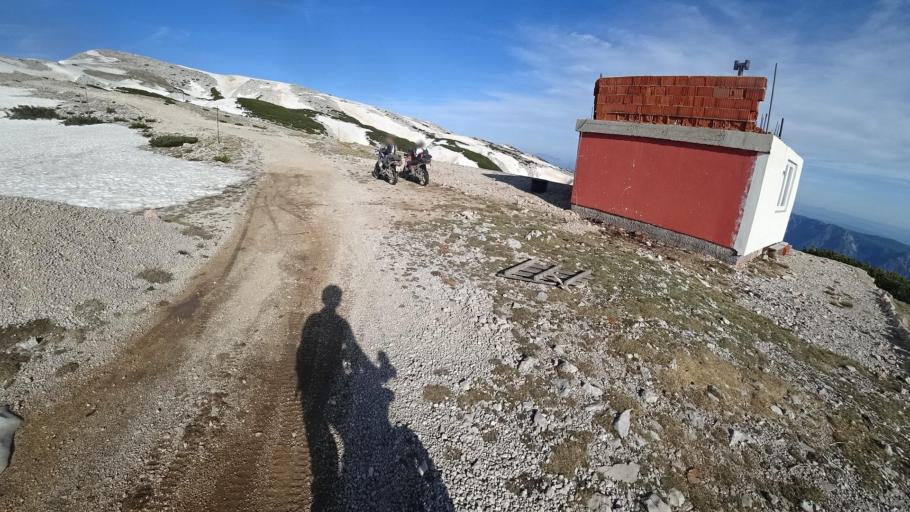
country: BA
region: Federation of Bosnia and Herzegovina
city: Kocerin
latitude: 43.5998
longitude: 17.5444
